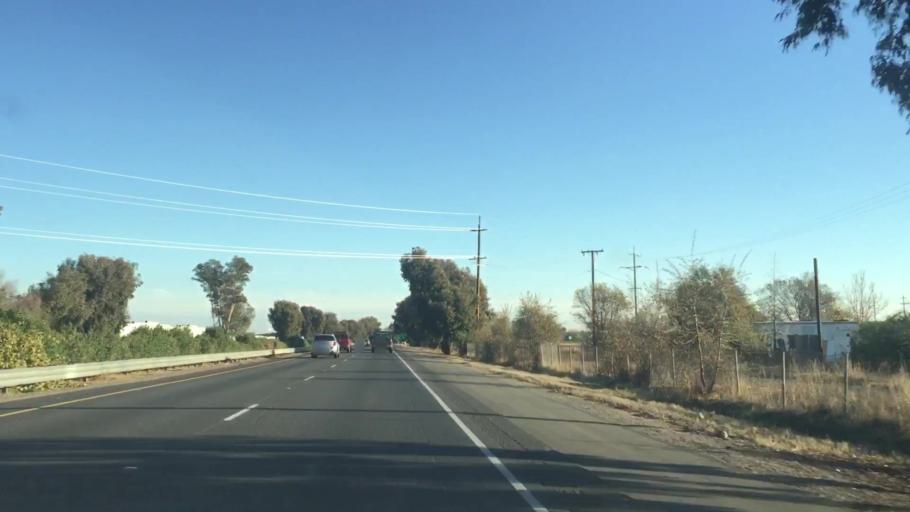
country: US
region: California
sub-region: Yuba County
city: Linda
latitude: 39.1176
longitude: -121.5660
